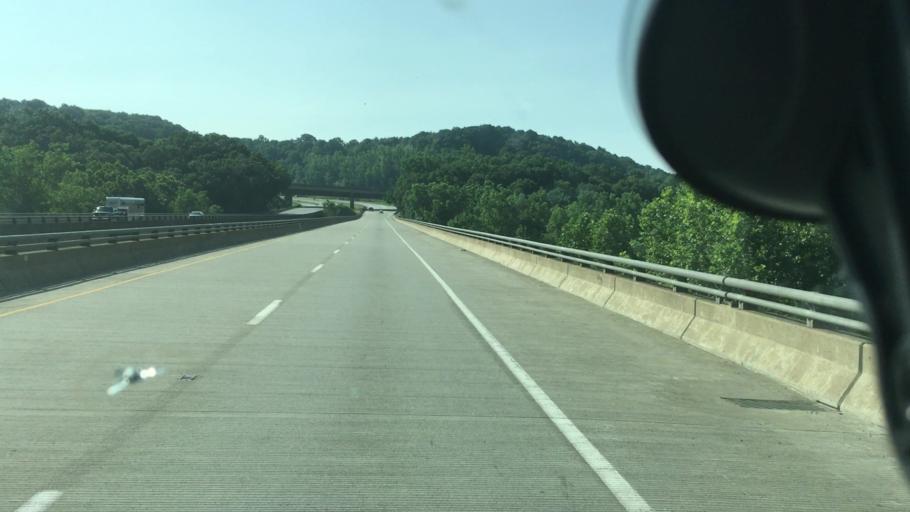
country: US
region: Pennsylvania
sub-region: Lawrence County
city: Oakland
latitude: 40.9724
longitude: -80.3688
